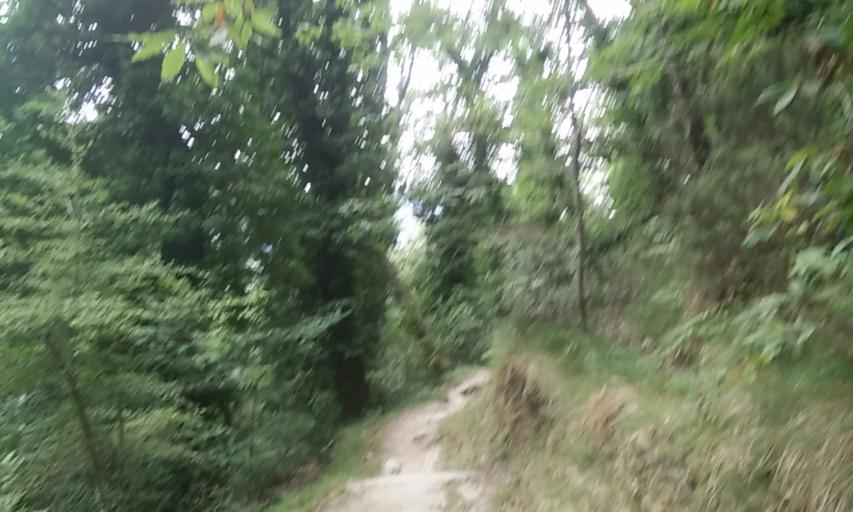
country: IT
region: Tuscany
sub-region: Provincia di Lucca
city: Pontestazzemese
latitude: 43.9960
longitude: 10.3260
